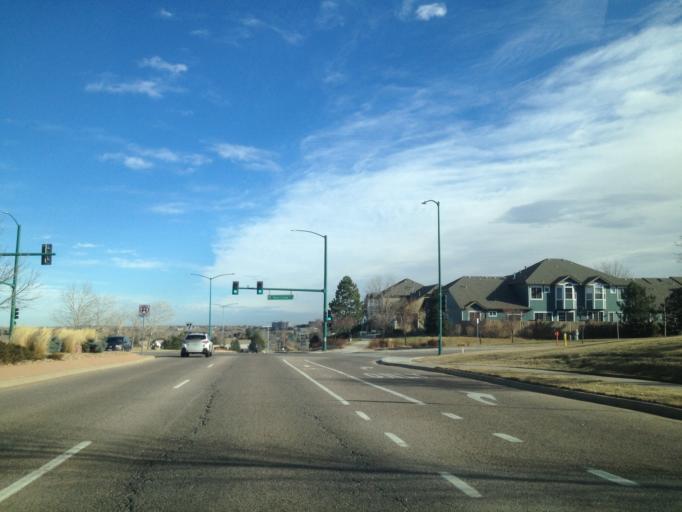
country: US
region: Colorado
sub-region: Boulder County
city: Superior
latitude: 39.9291
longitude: -105.1538
